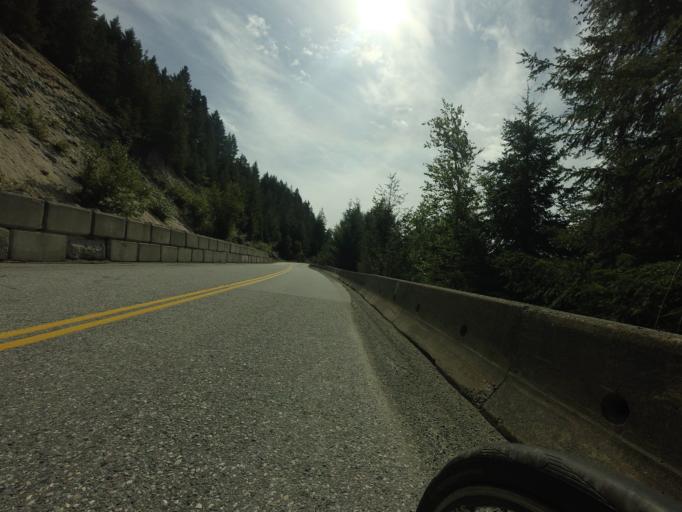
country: CA
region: British Columbia
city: Pemberton
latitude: 50.3019
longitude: -122.5881
